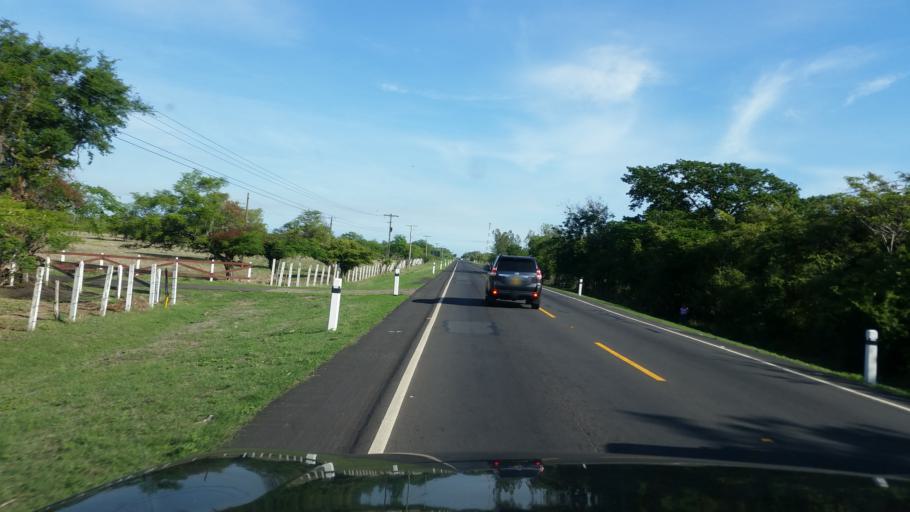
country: NI
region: Leon
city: La Paz Centro
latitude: 12.2904
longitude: -86.7613
